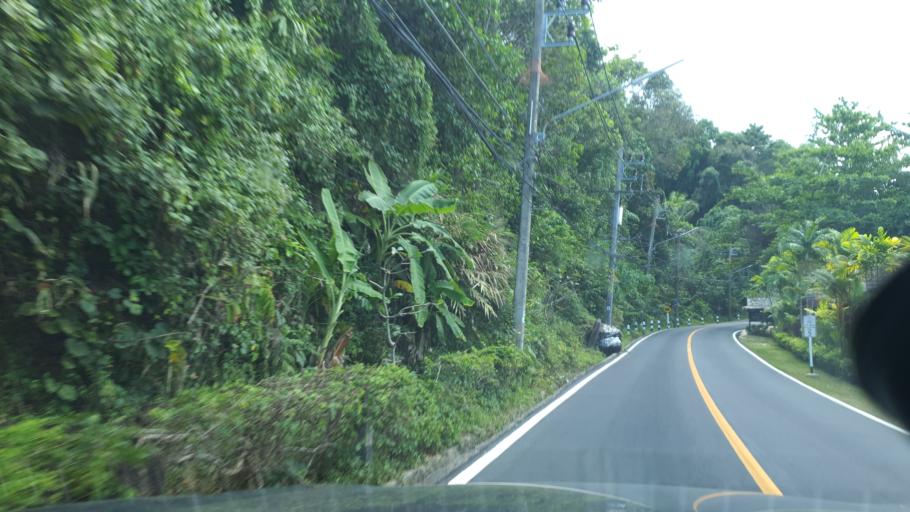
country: TH
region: Phuket
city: Thalang
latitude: 8.0464
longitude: 98.2784
